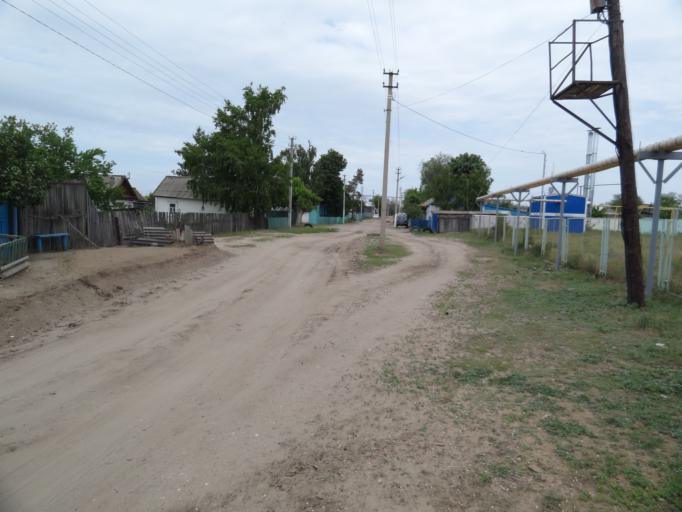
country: RU
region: Saratov
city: Privolzhskiy
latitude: 51.1802
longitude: 45.9178
